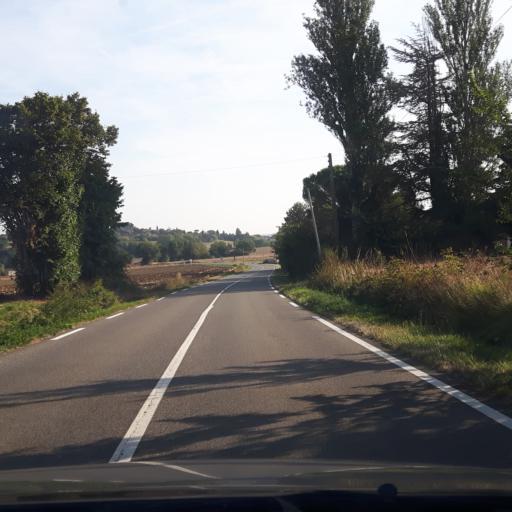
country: FR
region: Midi-Pyrenees
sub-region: Departement de la Haute-Garonne
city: Montjoire
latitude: 43.7606
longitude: 1.5233
